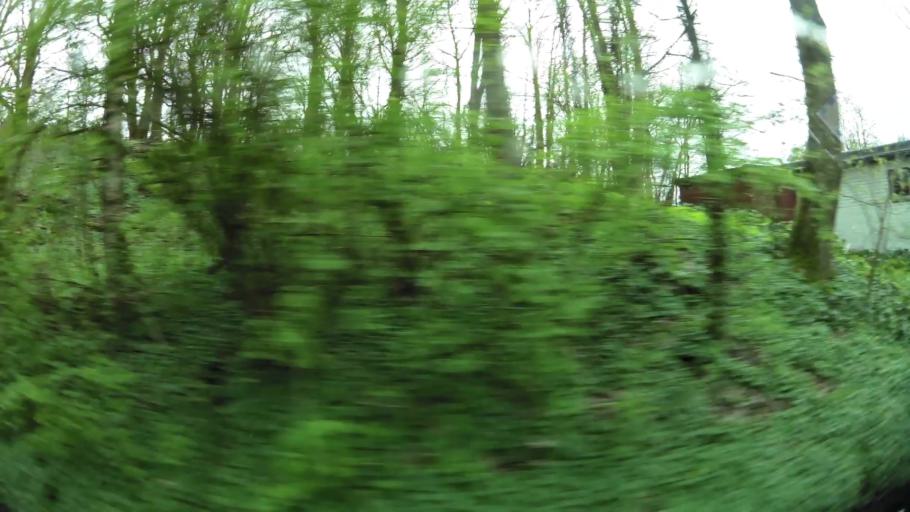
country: DK
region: Central Jutland
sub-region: Holstebro Kommune
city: Vinderup
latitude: 56.4087
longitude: 8.7631
